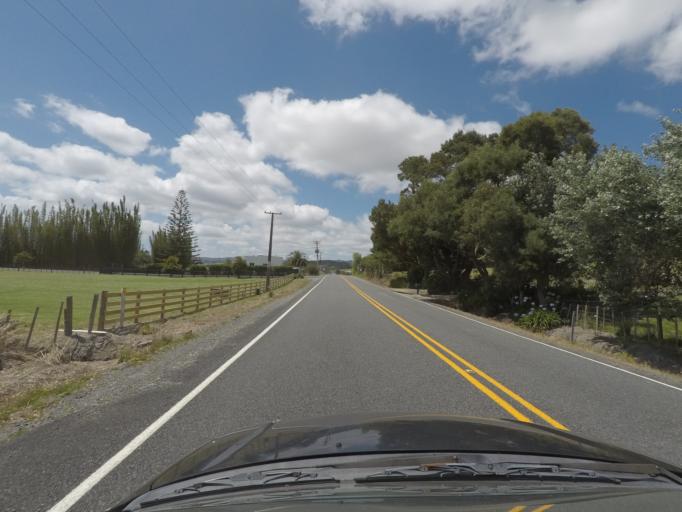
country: NZ
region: Northland
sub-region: Whangarei
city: Ruakaka
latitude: -36.0038
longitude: 174.4774
